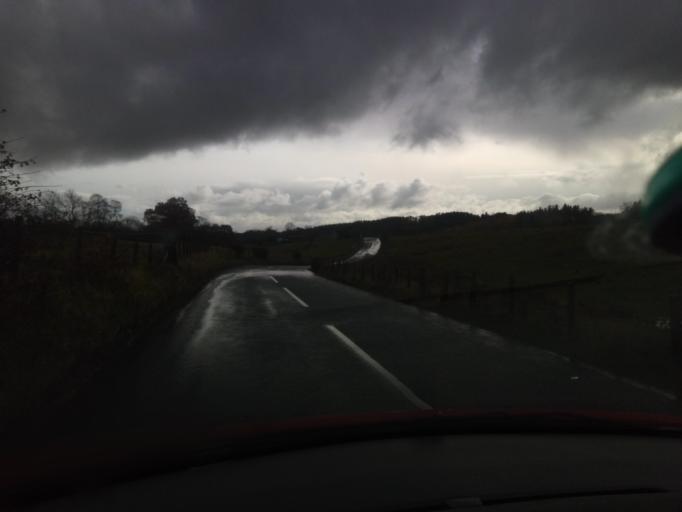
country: GB
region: England
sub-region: Northumberland
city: Birtley
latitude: 55.1090
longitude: -2.2401
